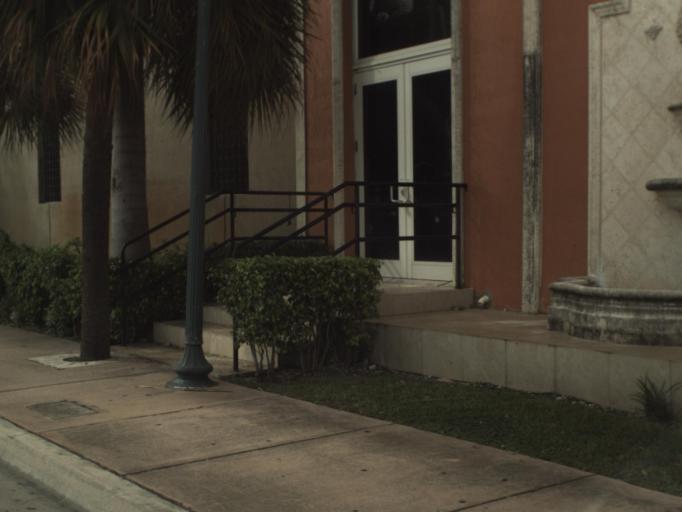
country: US
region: Florida
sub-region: Miami-Dade County
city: West Miami
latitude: 25.7633
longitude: -80.2988
